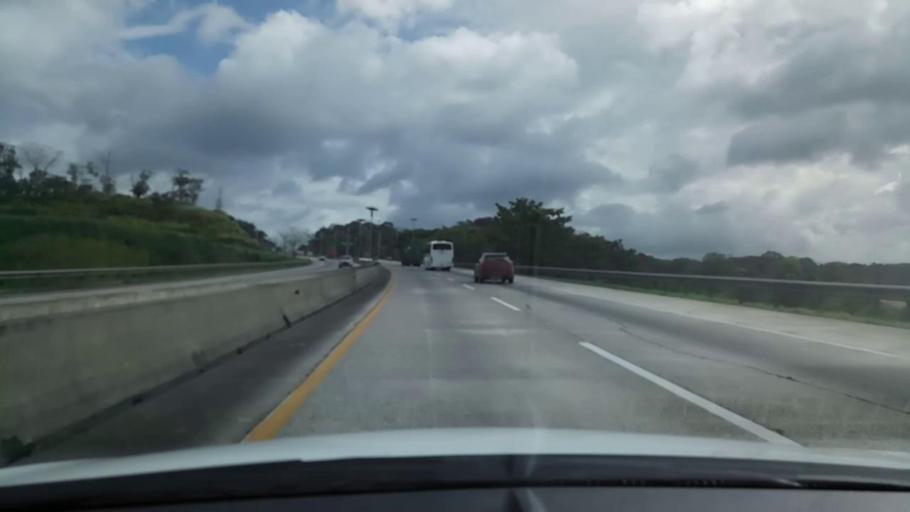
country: PA
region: Panama
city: Chilibre
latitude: 9.1280
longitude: -79.6216
